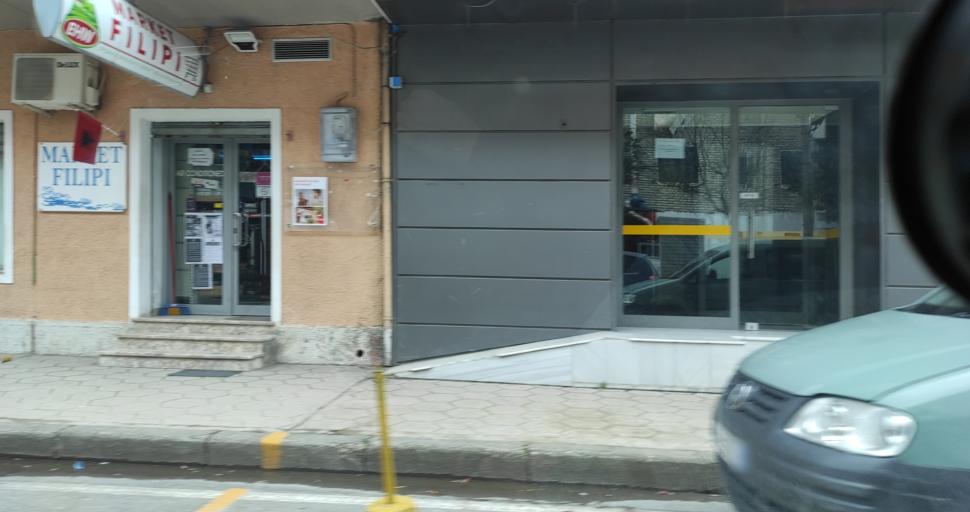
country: AL
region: Lezhe
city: Shengjin
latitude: 41.8141
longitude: 19.5920
